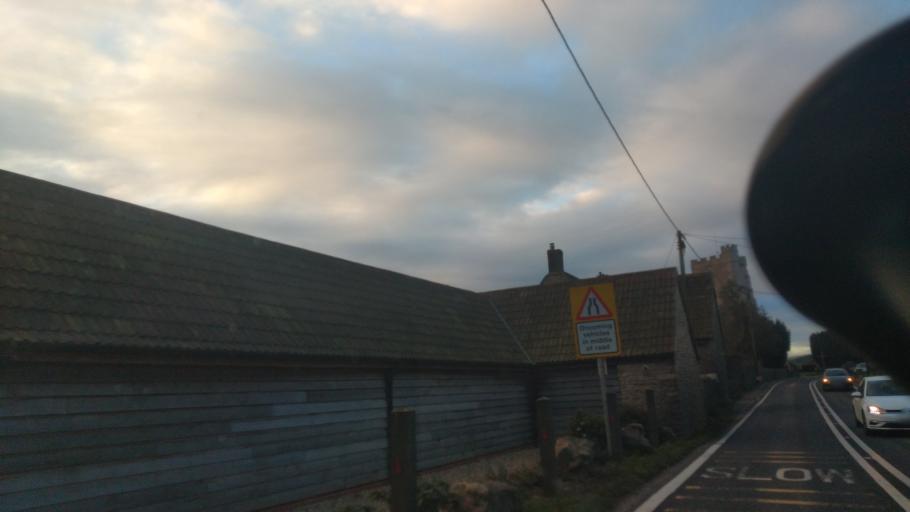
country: GB
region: England
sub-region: Wiltshire
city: Wingfield
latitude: 51.2802
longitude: -2.2756
